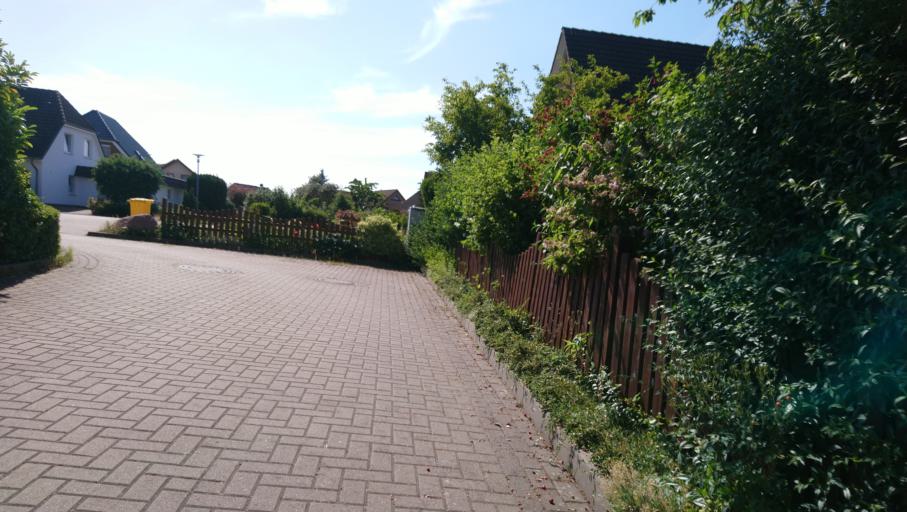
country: DE
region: Mecklenburg-Vorpommern
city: Roggentin
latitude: 54.0838
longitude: 12.1853
